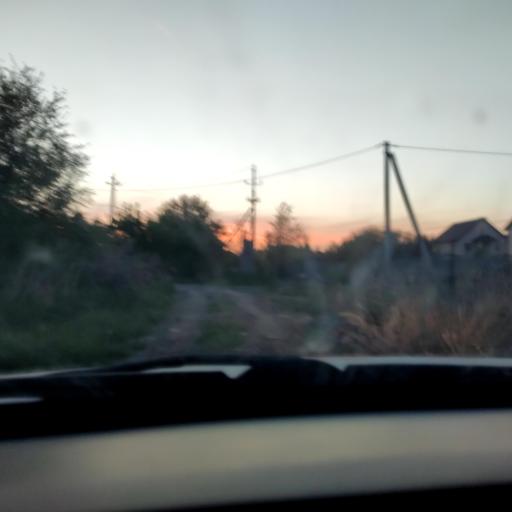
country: RU
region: Samara
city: Samara
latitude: 53.1306
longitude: 50.2405
